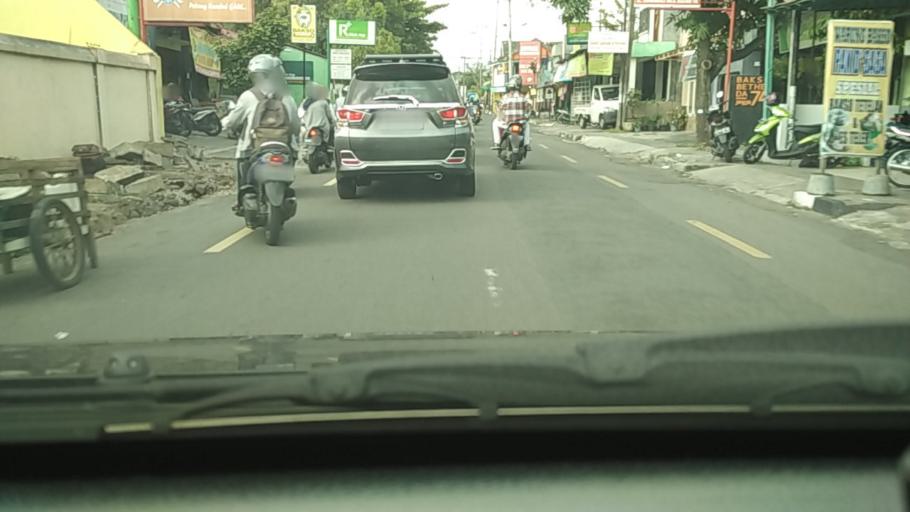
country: ID
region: Daerah Istimewa Yogyakarta
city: Yogyakarta
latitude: -7.7921
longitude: 110.3861
